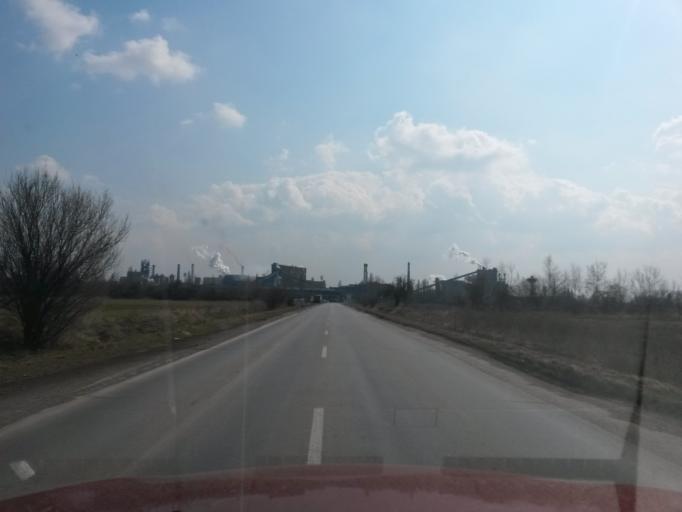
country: SK
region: Kosicky
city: Kosice
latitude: 48.6194
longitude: 21.1775
